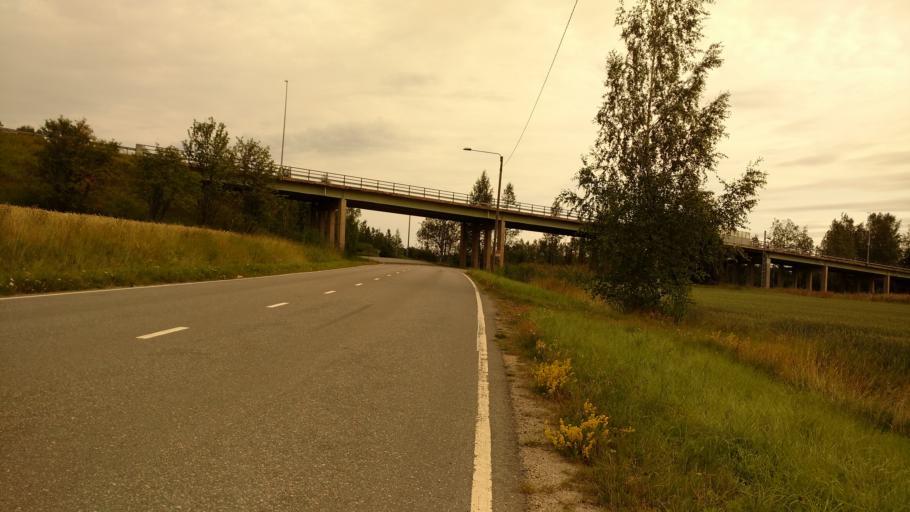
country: FI
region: Varsinais-Suomi
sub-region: Turku
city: Piikkioe
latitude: 60.4286
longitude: 22.5377
